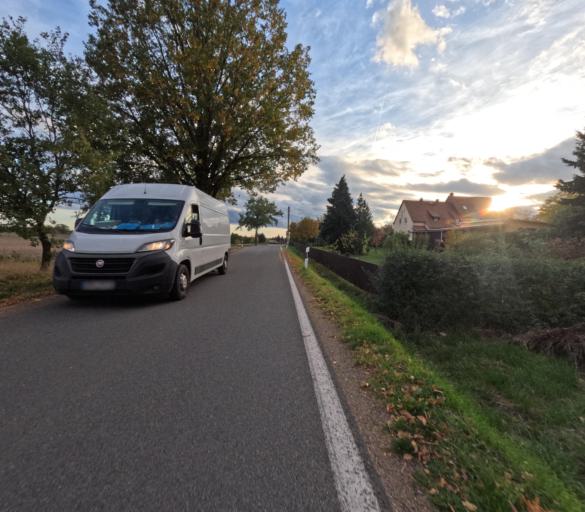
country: DE
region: Saxony
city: Grossbardau
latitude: 51.2467
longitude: 12.6702
